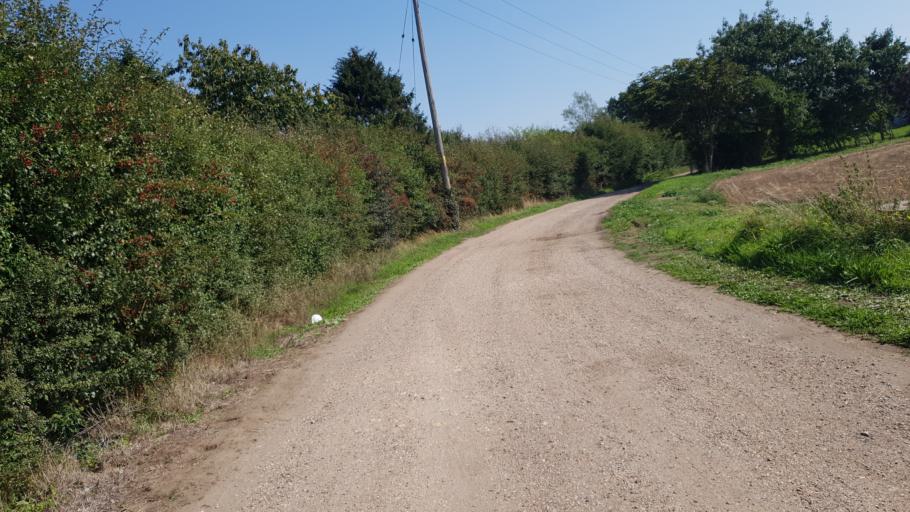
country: GB
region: England
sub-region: Essex
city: Wivenhoe
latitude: 51.9215
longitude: 0.9760
